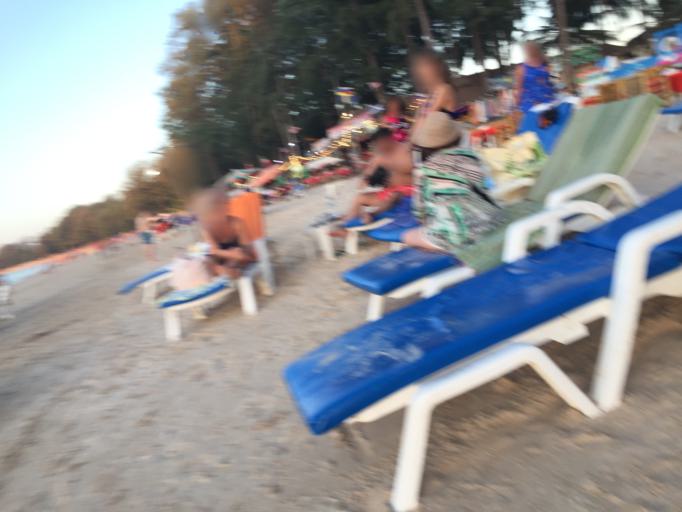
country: TH
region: Phuket
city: Thalang
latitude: 7.9868
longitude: 98.2875
